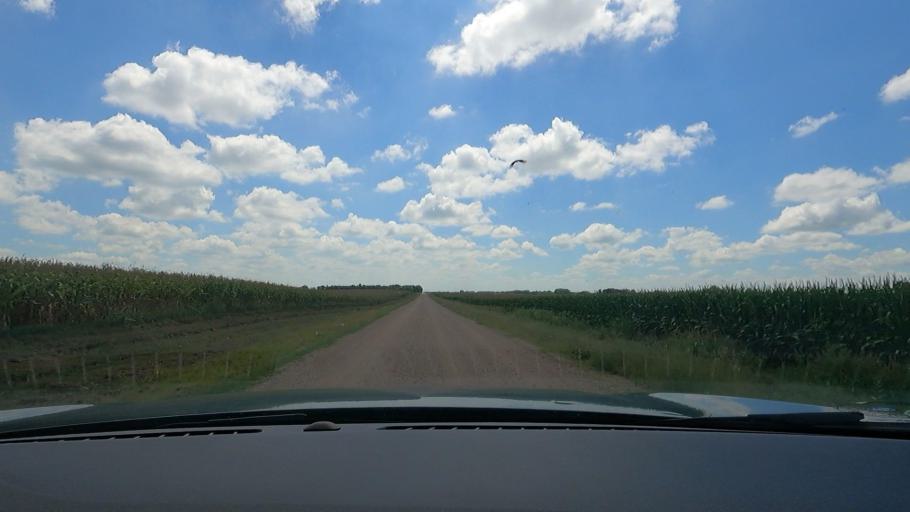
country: US
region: Nebraska
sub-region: Saunders County
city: Wahoo
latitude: 41.2743
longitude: -96.5419
